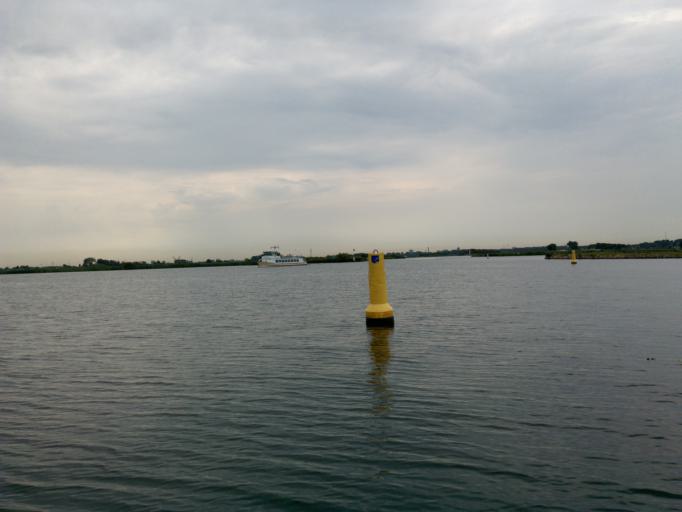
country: NL
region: South Holland
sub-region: Gemeente Teylingen
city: Sassenheim
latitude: 52.2101
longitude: 4.5340
